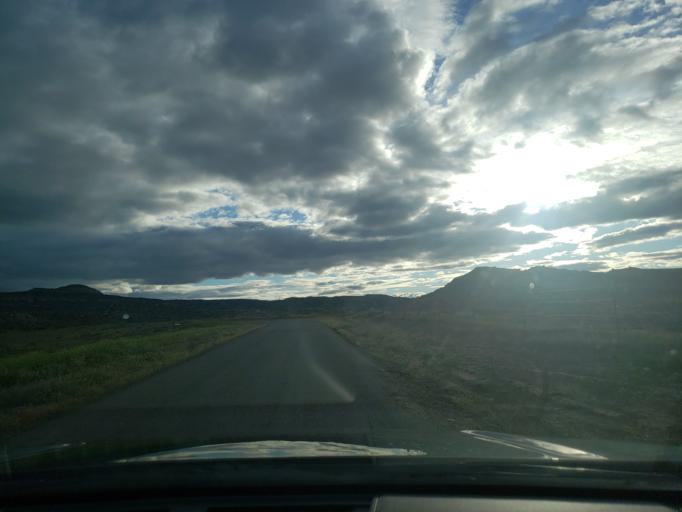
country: US
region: Colorado
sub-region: Mesa County
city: Fruita
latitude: 39.1428
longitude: -108.7457
